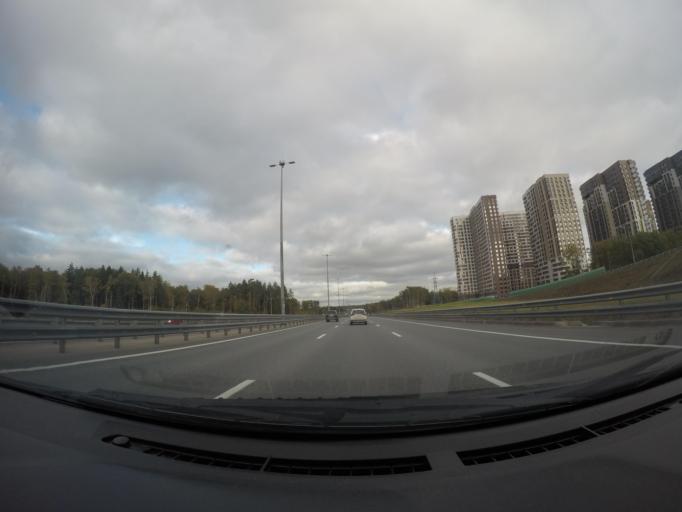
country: RU
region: Moskovskaya
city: Lesnoy Gorodok
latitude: 55.6785
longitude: 37.2310
